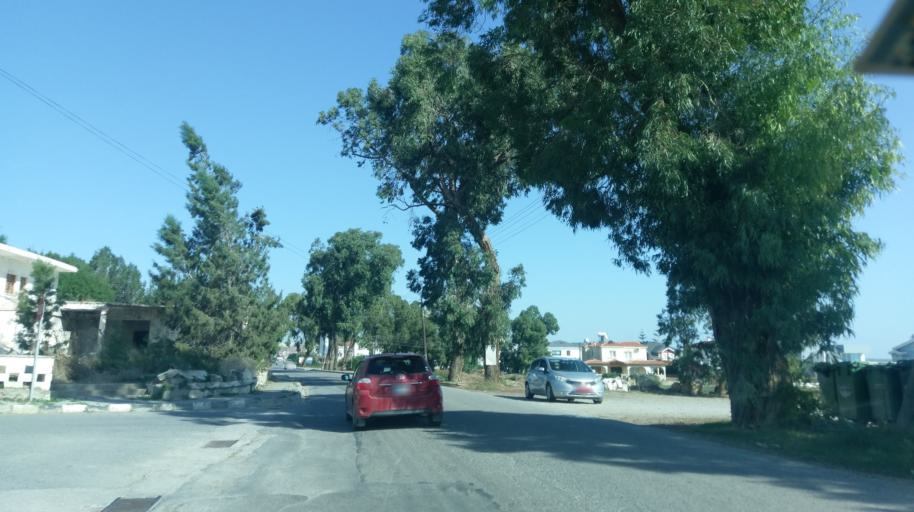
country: CY
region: Ammochostos
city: Trikomo
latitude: 35.3144
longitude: 33.9528
